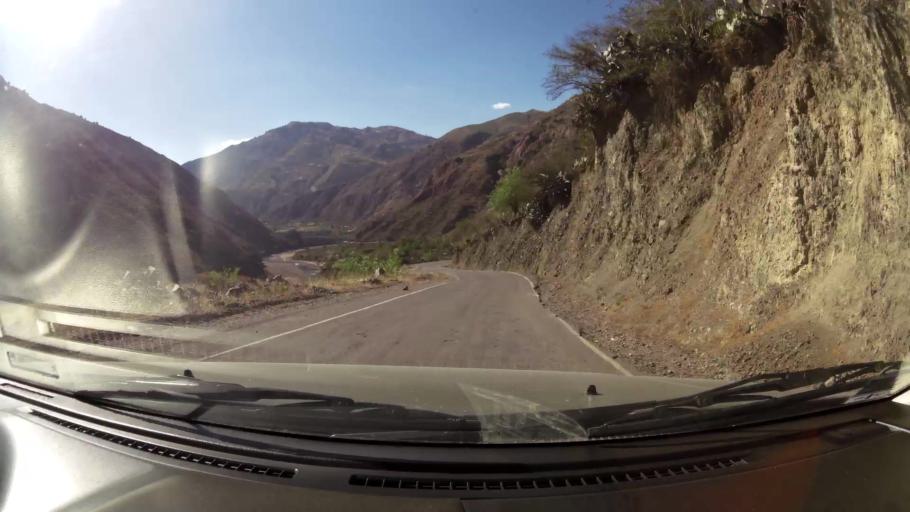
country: PE
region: Huancavelica
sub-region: Provincia de Acobamba
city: Pomacocha
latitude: -12.7849
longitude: -74.4983
